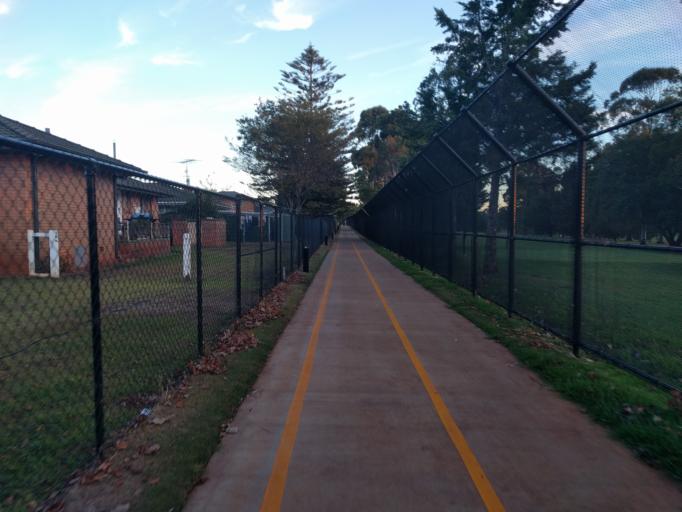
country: AU
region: Queensland
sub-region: Toowoomba
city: Toowoomba
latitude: -27.5785
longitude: 151.9481
